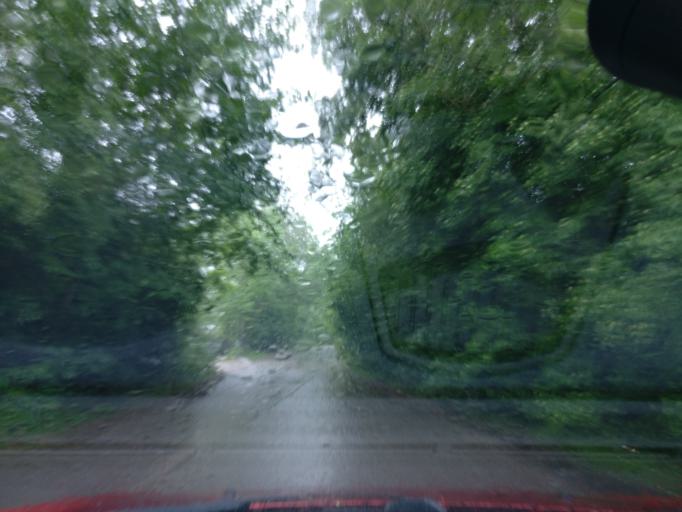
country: DE
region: Bavaria
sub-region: Upper Bavaria
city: Dachau
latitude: 48.2464
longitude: 11.4596
